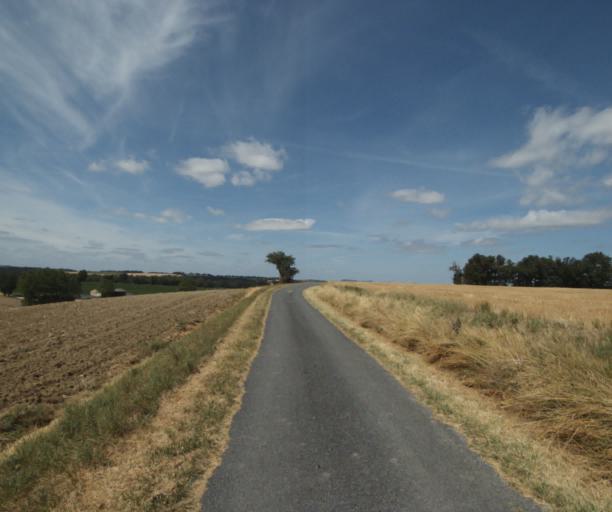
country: FR
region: Midi-Pyrenees
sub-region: Departement du Tarn
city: Dourgne
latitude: 43.4970
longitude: 2.0984
